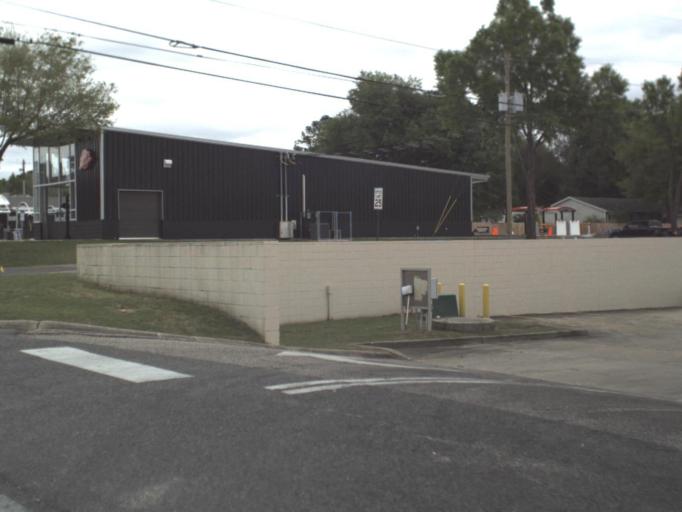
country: US
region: Florida
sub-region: Escambia County
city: Bellview
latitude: 30.4610
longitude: -87.2981
